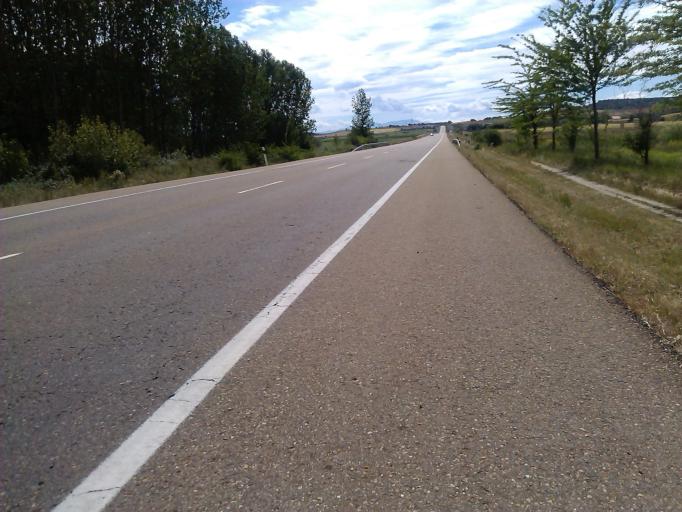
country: ES
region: Castille and Leon
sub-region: Provincia de Leon
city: Villarejo de Orbigo
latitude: 42.4538
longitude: -5.9104
